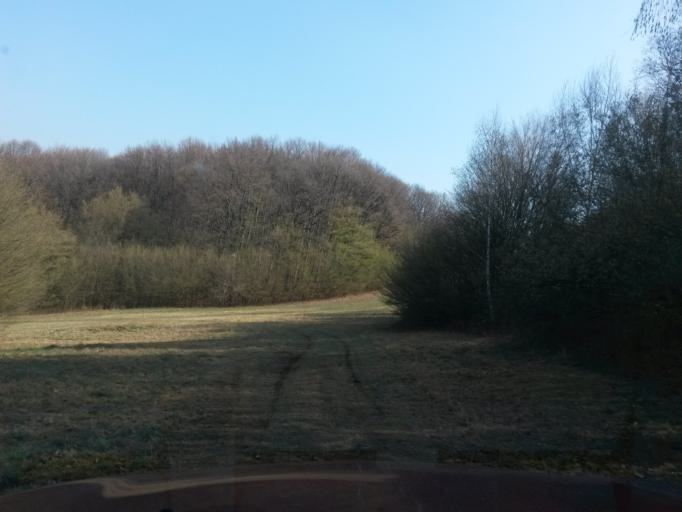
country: SK
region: Presovsky
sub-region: Okres Presov
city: Presov
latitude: 48.9285
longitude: 21.1477
